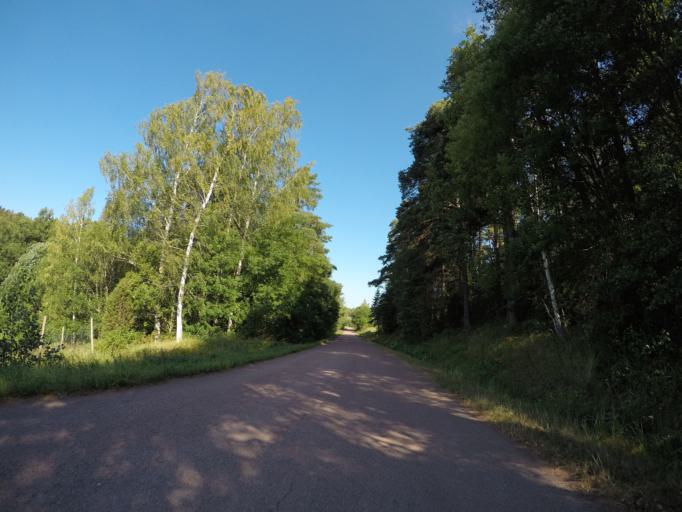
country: AX
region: Alands landsbygd
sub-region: Finstroem
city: Finstroem
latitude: 60.2684
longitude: 19.9280
